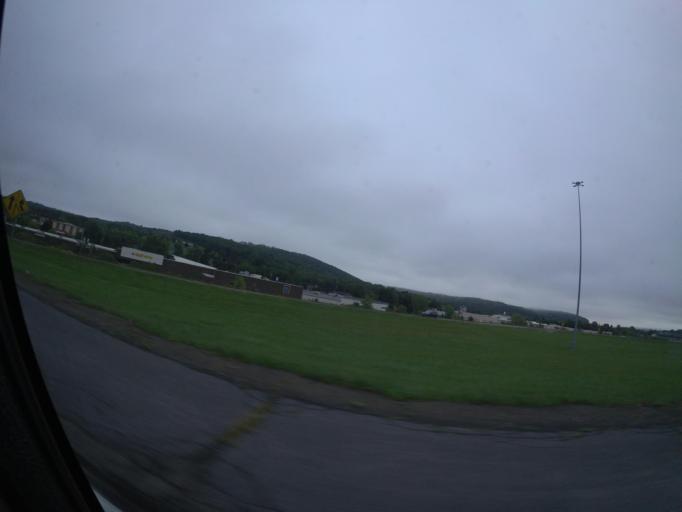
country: US
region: New York
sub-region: Broome County
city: Johnson City
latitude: 42.1215
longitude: -75.9701
